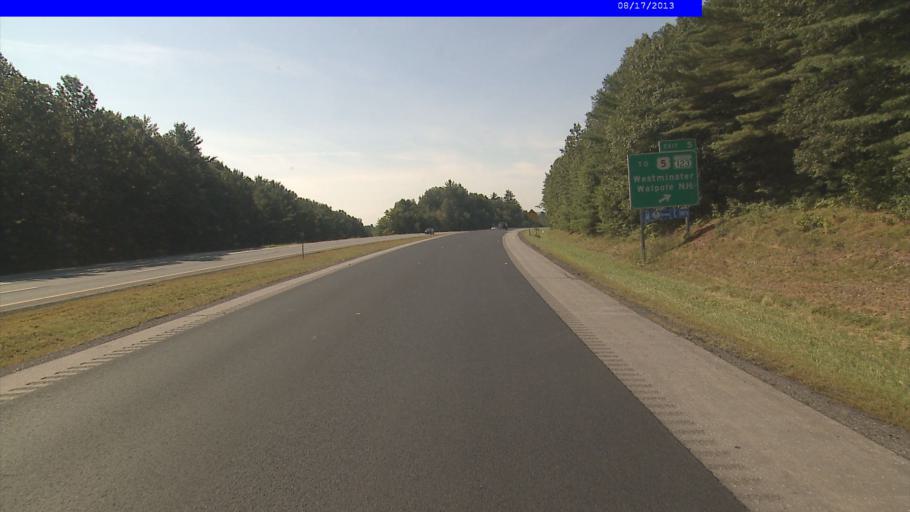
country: US
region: Vermont
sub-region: Windham County
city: Bellows Falls
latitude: 43.0955
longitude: -72.4541
